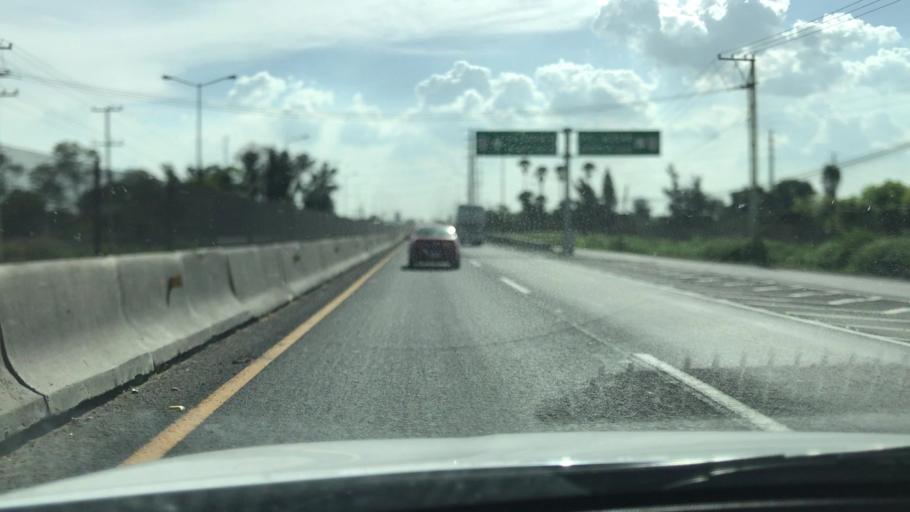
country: MX
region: Guanajuato
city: Villagran
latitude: 20.5088
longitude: -100.9867
